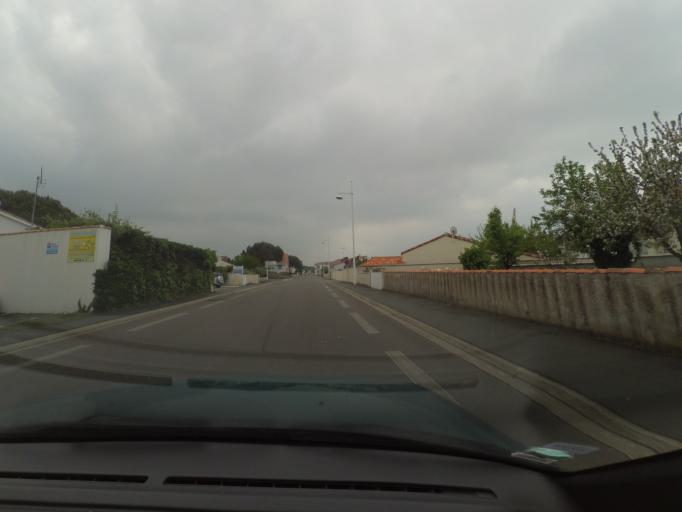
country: FR
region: Pays de la Loire
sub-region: Departement de la Vendee
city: Angles
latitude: 46.3338
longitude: -1.3245
